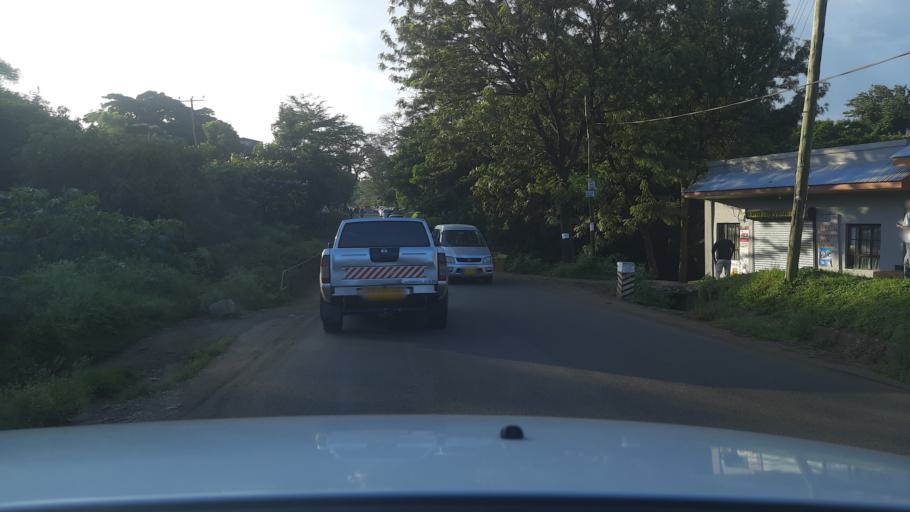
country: TZ
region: Arusha
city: Arusha
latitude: -3.3794
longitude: 36.7062
